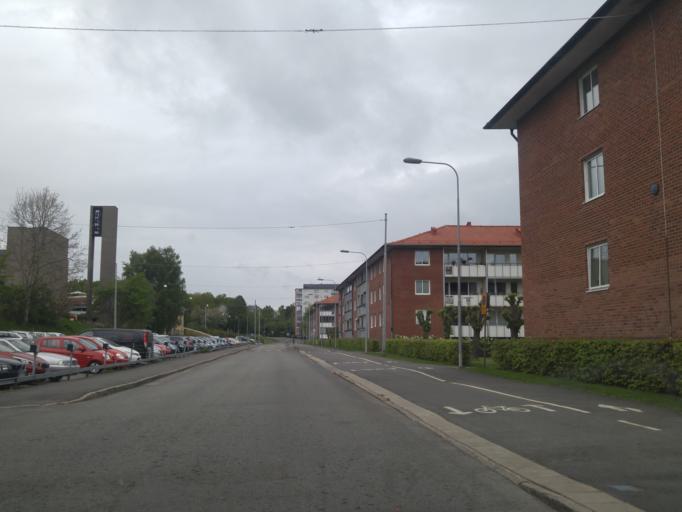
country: SE
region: Vaestra Goetaland
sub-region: Goteborg
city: Majorna
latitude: 57.6700
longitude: 11.9315
